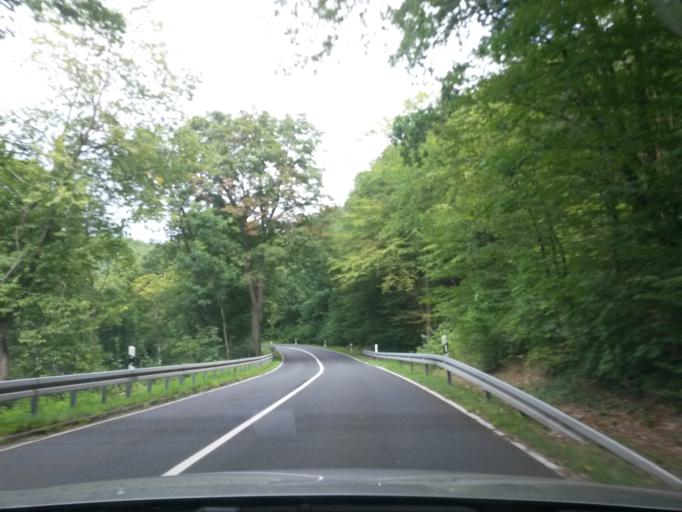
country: DE
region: Brandenburg
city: Liepe
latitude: 52.8631
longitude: 14.0012
